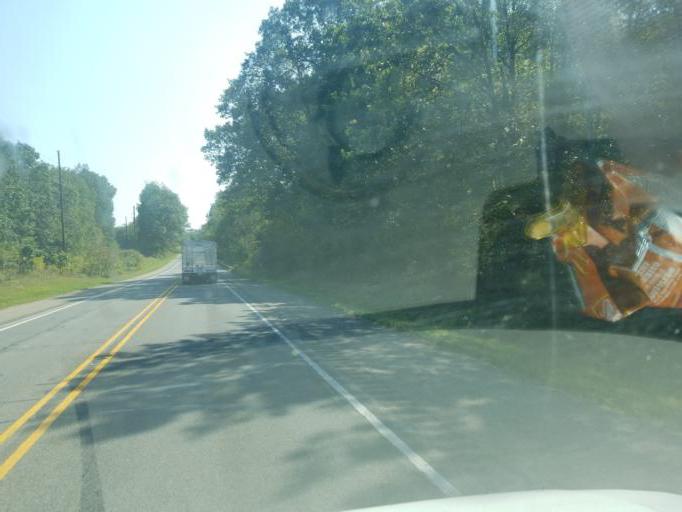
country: US
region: Indiana
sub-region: Steuben County
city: Angola
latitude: 41.6386
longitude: -85.1568
